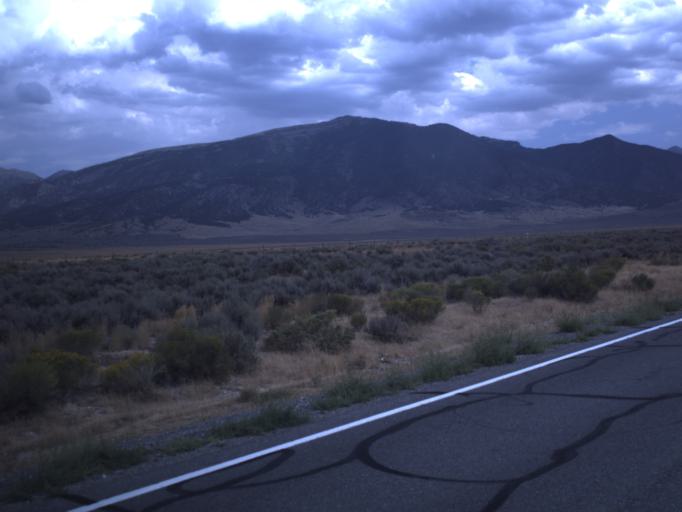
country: US
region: Utah
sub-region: Tooele County
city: Tooele
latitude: 40.3788
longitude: -112.3808
